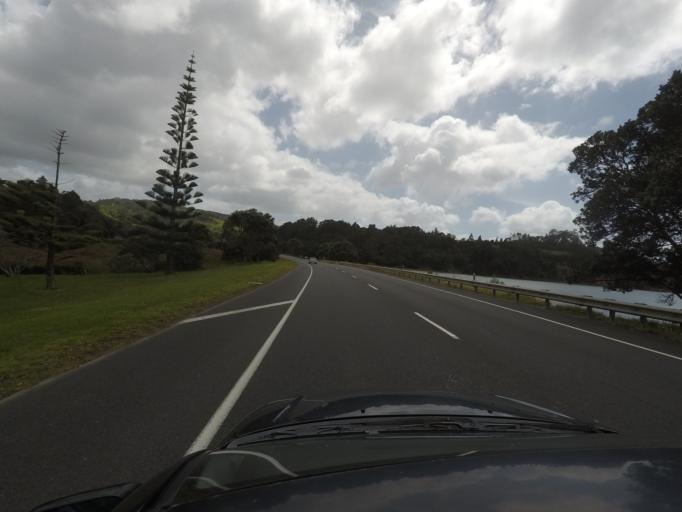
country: NZ
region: Auckland
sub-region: Auckland
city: Warkworth
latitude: -36.5642
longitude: 174.6954
